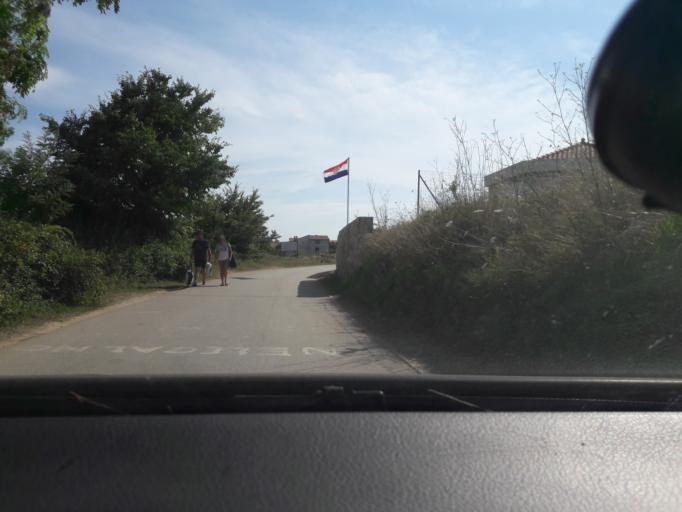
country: HR
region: Zadarska
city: Nin
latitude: 44.2452
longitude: 15.1755
